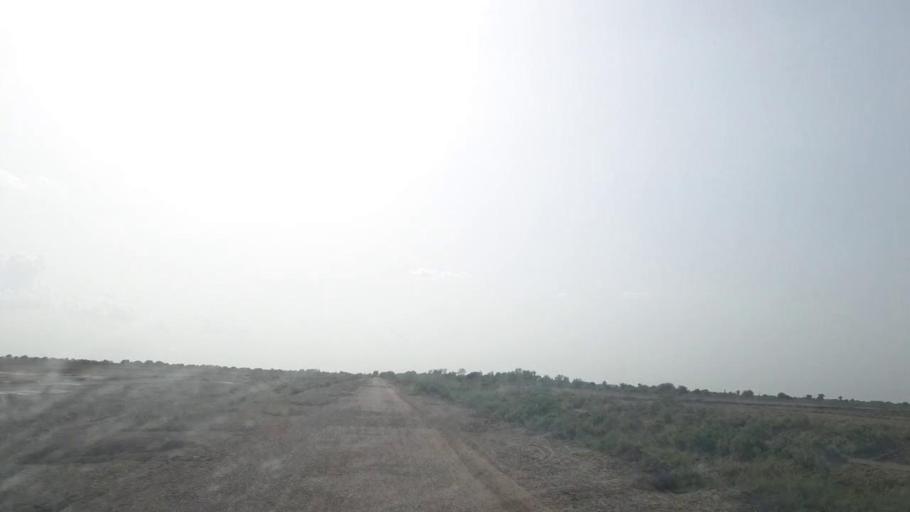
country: PK
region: Sindh
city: Tando Bago
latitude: 24.8186
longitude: 69.1397
